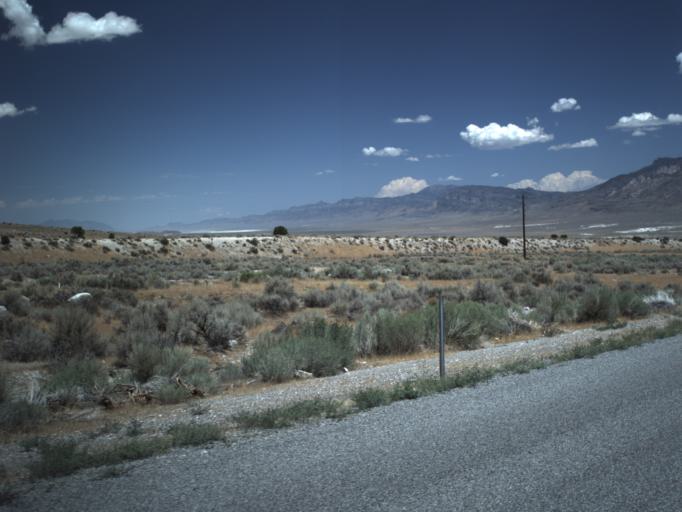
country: US
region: Utah
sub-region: Beaver County
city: Milford
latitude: 39.0864
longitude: -113.5577
